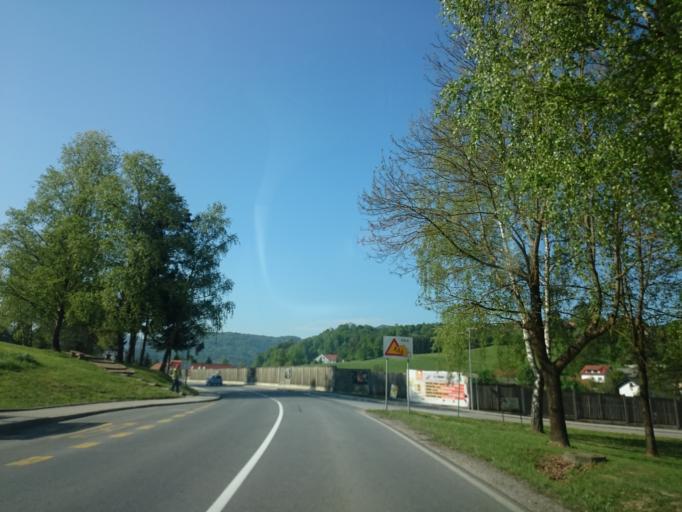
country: SI
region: Sentjur pri Celju
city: Sentjur
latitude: 46.2223
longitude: 15.3951
